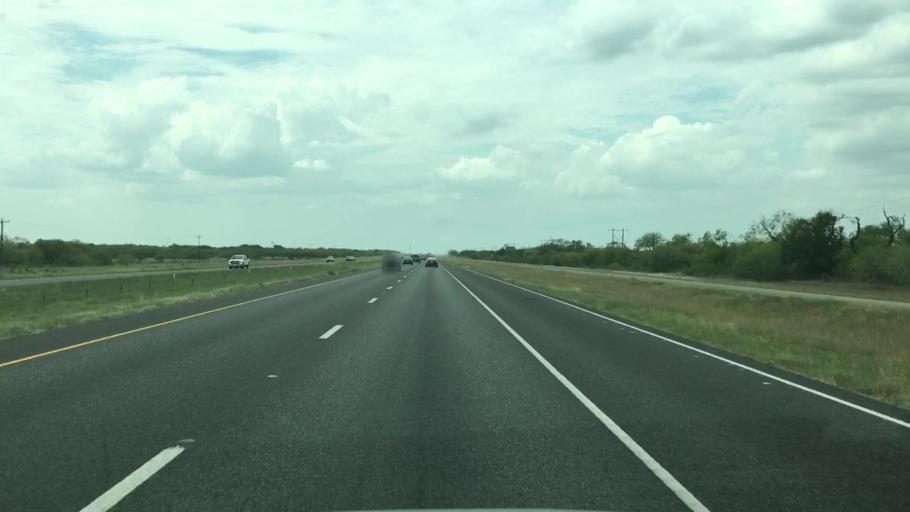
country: US
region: Texas
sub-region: Atascosa County
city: Pleasanton
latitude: 28.8023
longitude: -98.3432
